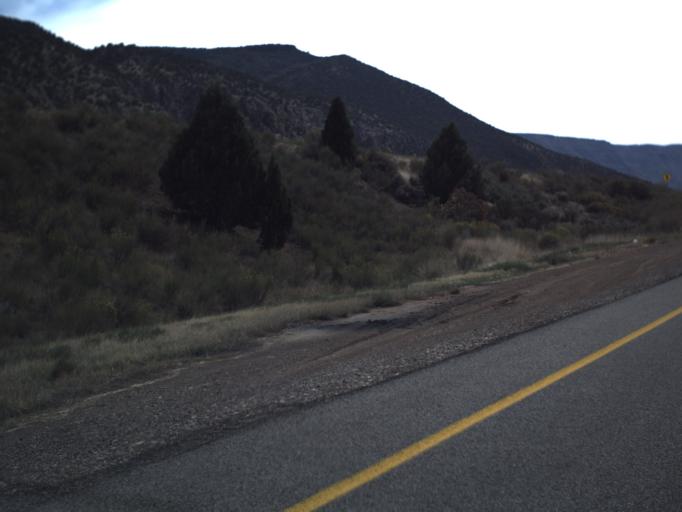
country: US
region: Utah
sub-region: Washington County
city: Toquerville
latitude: 37.4543
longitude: -113.2289
